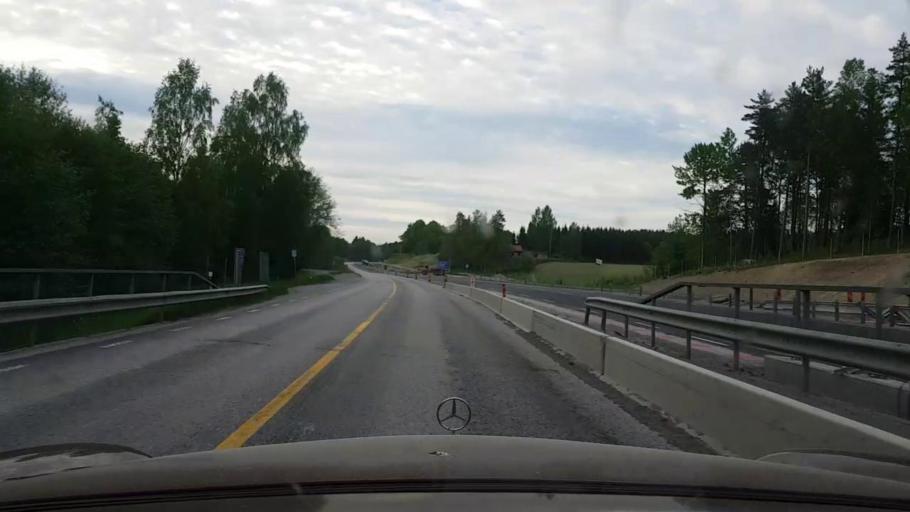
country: SE
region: OErebro
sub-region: Askersunds Kommun
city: Asbro
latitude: 58.9293
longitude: 15.0002
